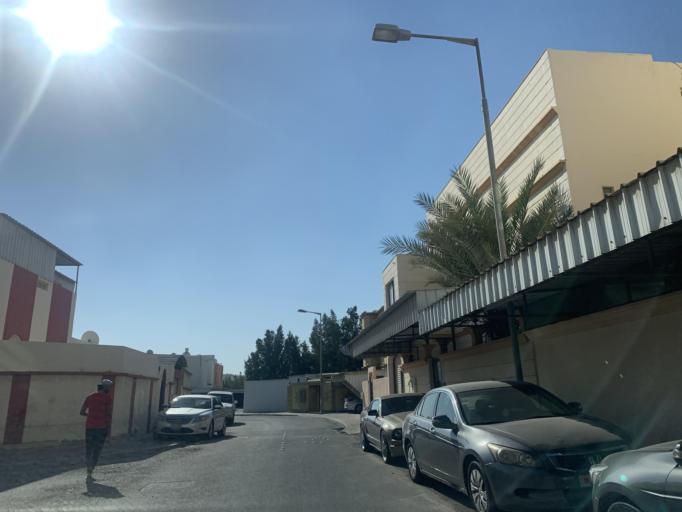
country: BH
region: Central Governorate
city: Madinat Hamad
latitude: 26.1171
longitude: 50.5076
